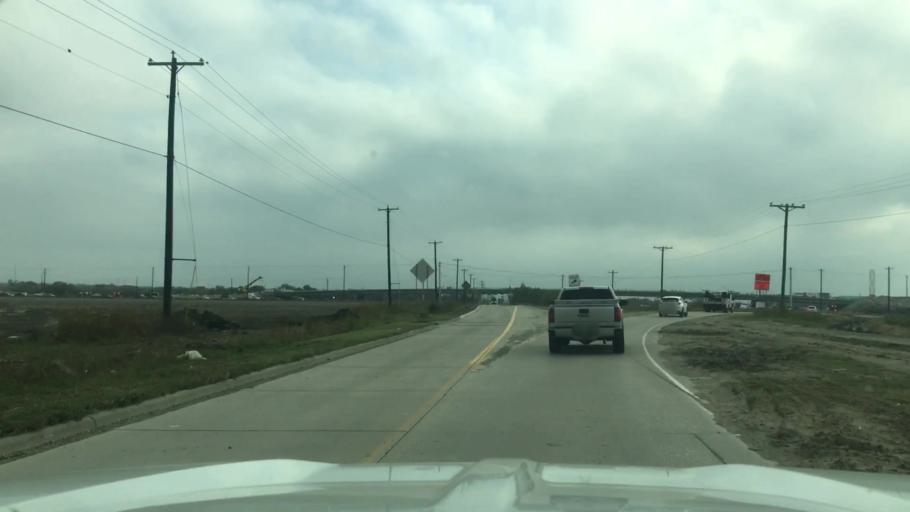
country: US
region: Texas
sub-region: Collin County
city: Prosper
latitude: 33.2231
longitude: -96.8196
